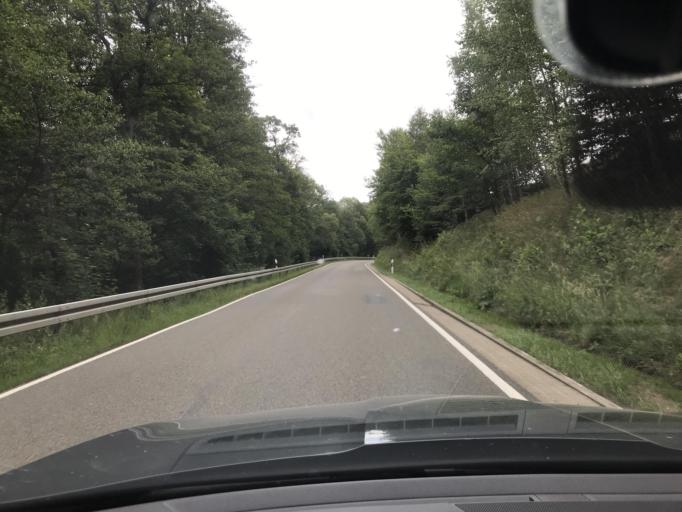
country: DE
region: Saxony-Anhalt
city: Harzgerode
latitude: 51.6399
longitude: 11.1046
